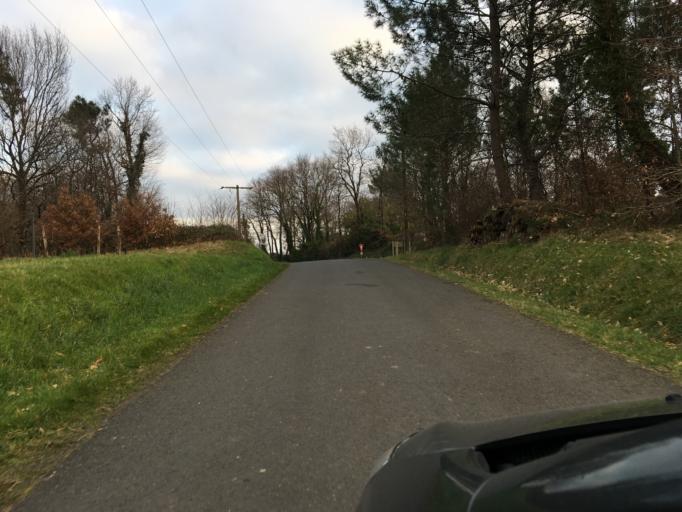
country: FR
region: Aquitaine
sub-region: Departement de la Gironde
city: Saint-Ciers-sur-Gironde
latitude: 45.3123
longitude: -0.6078
